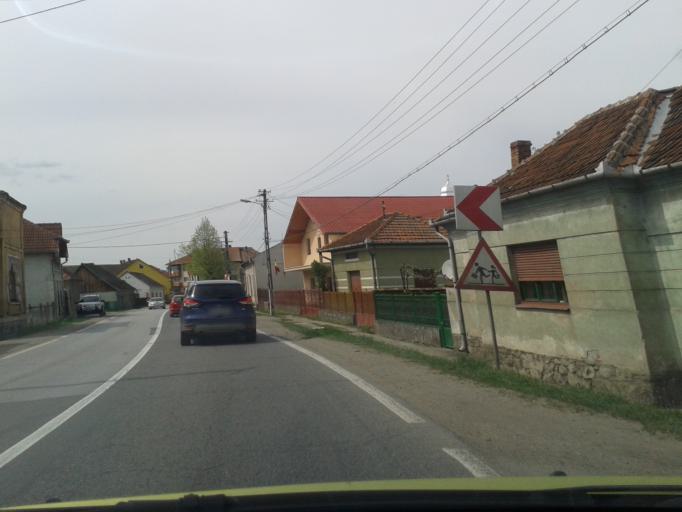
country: RO
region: Hunedoara
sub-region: Comuna Dobra
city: Dobra
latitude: 45.9110
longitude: 22.5742
